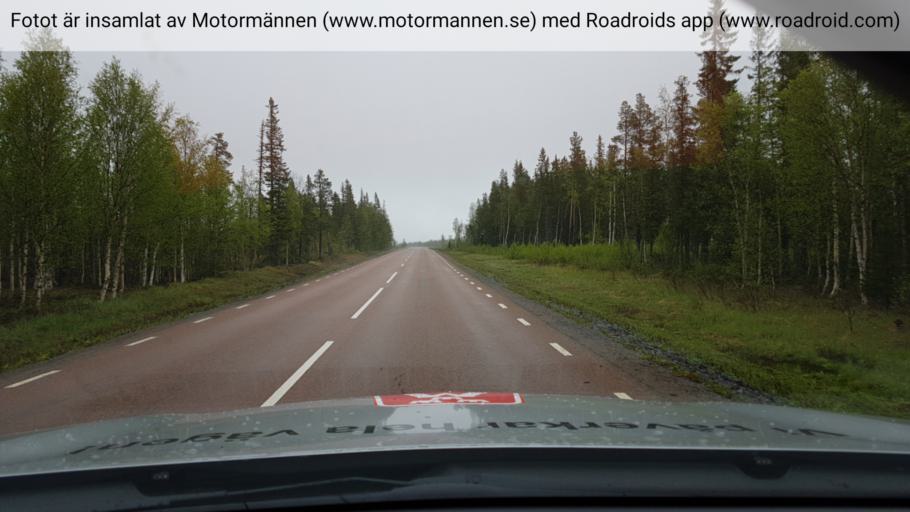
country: SE
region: Jaemtland
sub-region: Krokoms Kommun
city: Valla
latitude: 63.1310
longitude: 13.9357
